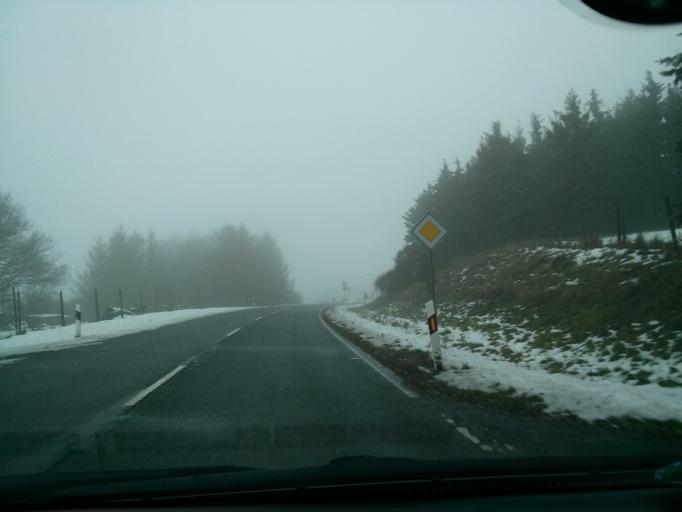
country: DE
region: Rheinland-Pfalz
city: Berg
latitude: 50.5643
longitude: 6.9619
